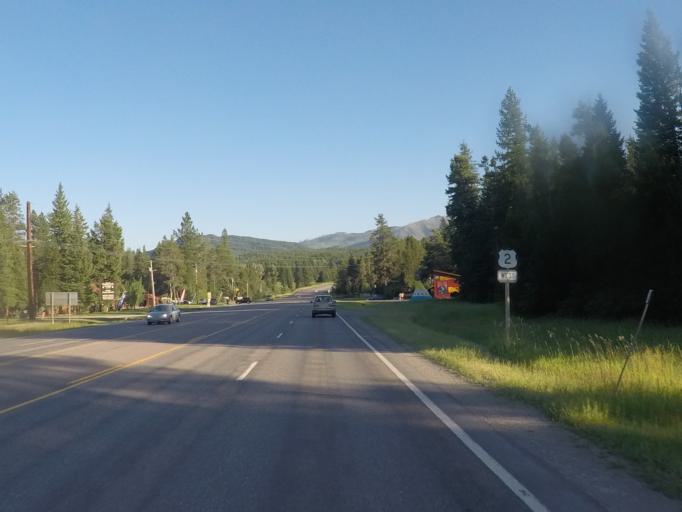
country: US
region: Montana
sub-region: Flathead County
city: Columbia Falls
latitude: 48.3996
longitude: -114.0423
